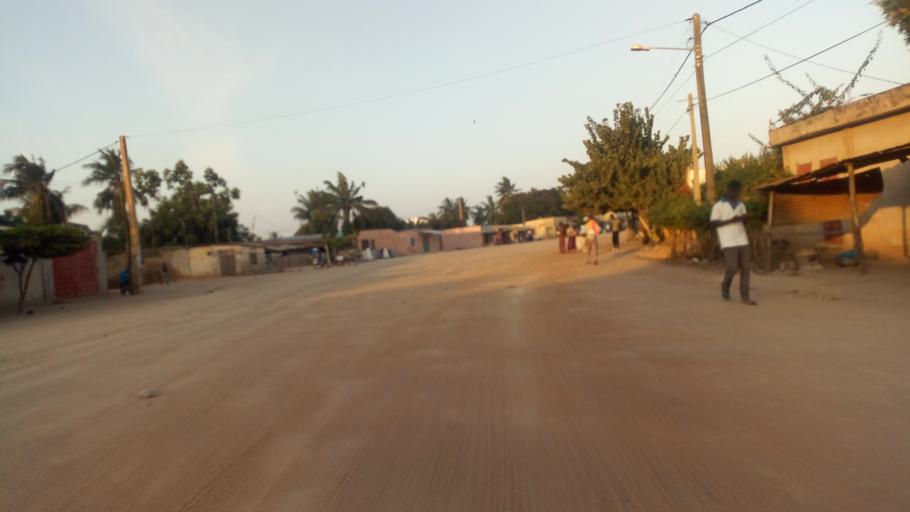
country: TG
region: Maritime
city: Lome
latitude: 6.1929
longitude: 1.1985
